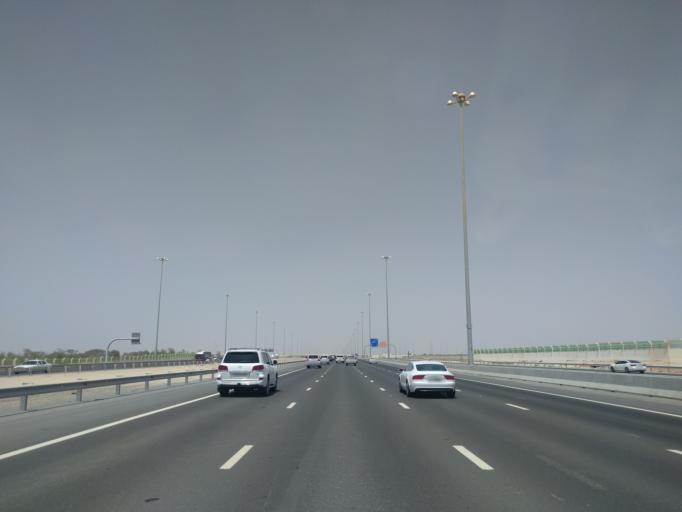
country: AE
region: Abu Dhabi
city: Abu Dhabi
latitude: 24.6867
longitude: 54.7737
